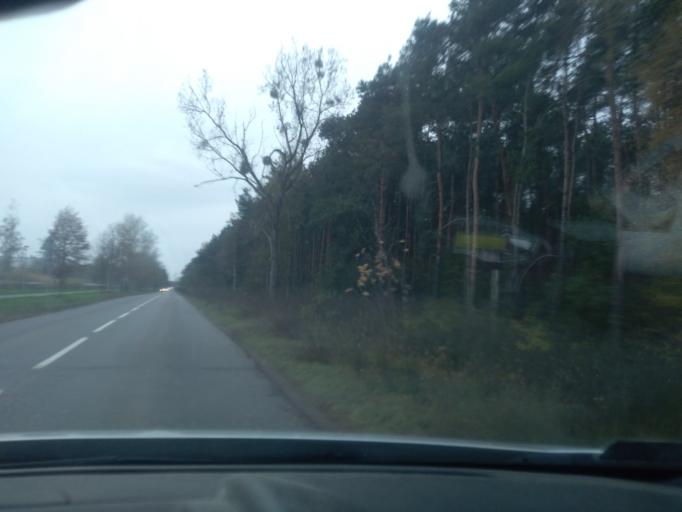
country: PL
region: Greater Poland Voivodeship
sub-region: Powiat poznanski
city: Murowana Goslina
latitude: 52.5550
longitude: 16.9745
